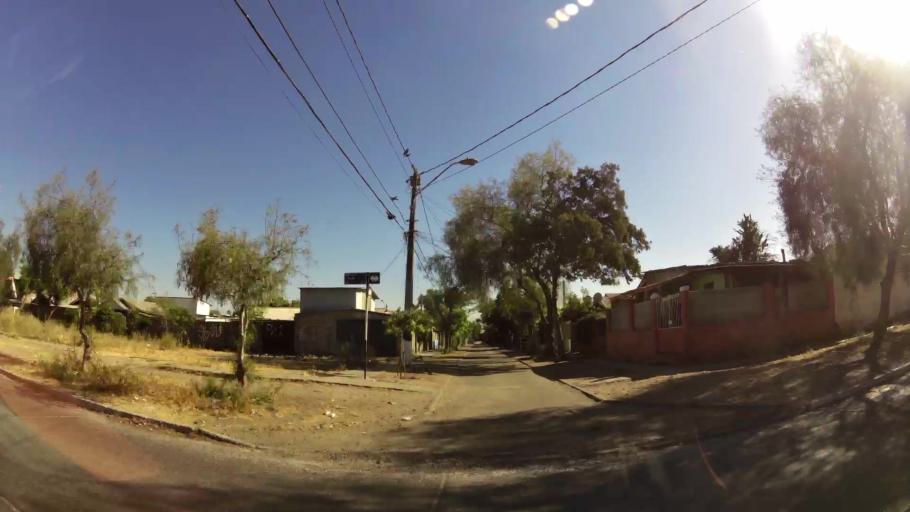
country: CL
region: Santiago Metropolitan
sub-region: Provincia de Maipo
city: San Bernardo
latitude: -33.5522
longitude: -70.6868
